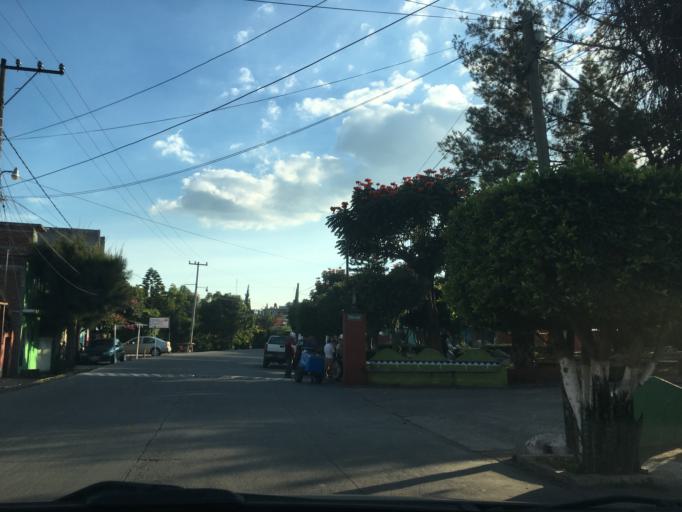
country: MX
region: Michoacan
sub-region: Cuitzeo
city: San Juan Benito Juarez (San Juan Tararameo)
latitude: 19.8717
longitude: -101.1422
